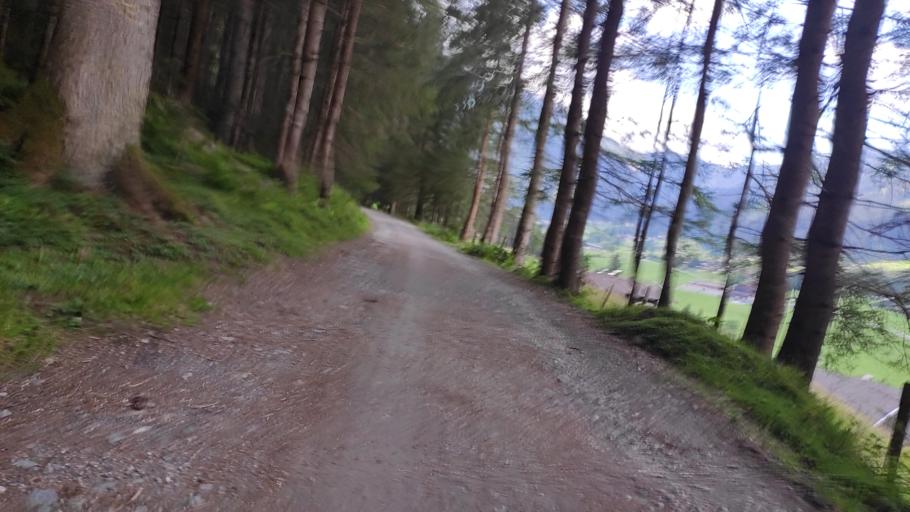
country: AT
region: Salzburg
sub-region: Politischer Bezirk Zell am See
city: Krimml
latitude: 47.2308
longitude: 12.1960
